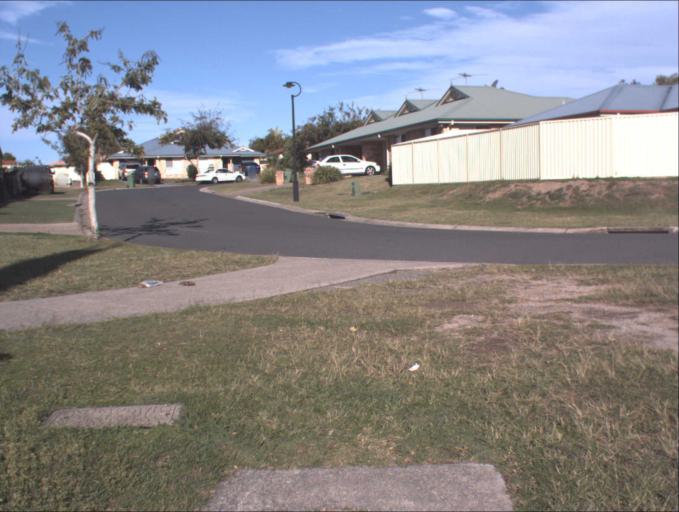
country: AU
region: Queensland
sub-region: Logan
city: Logan Reserve
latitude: -27.6948
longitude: 153.0903
